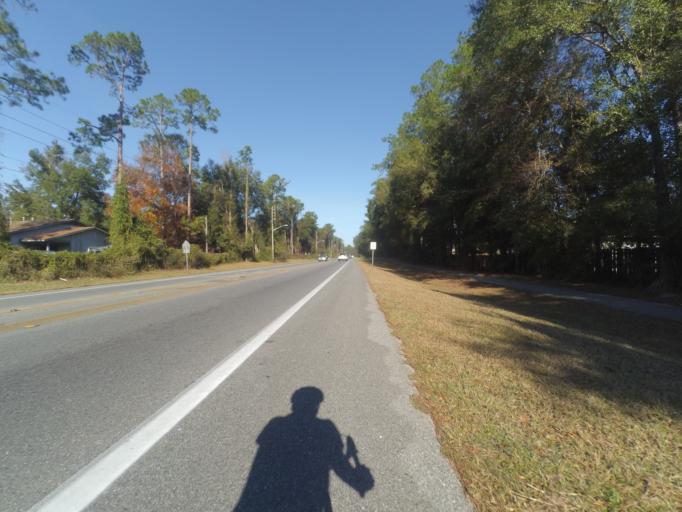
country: US
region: Florida
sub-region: Alachua County
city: Gainesville
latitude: 29.6333
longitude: -82.4150
